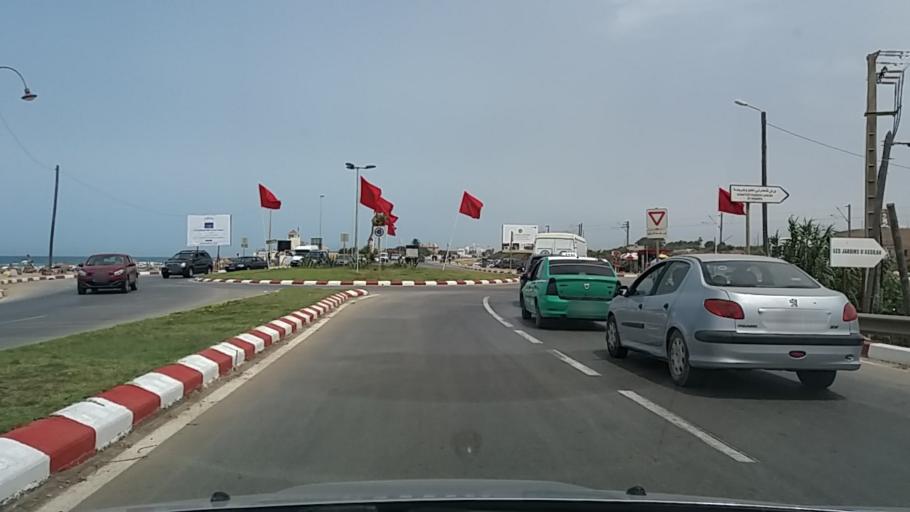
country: MA
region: Tanger-Tetouan
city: Asilah
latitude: 35.4764
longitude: -6.0260
